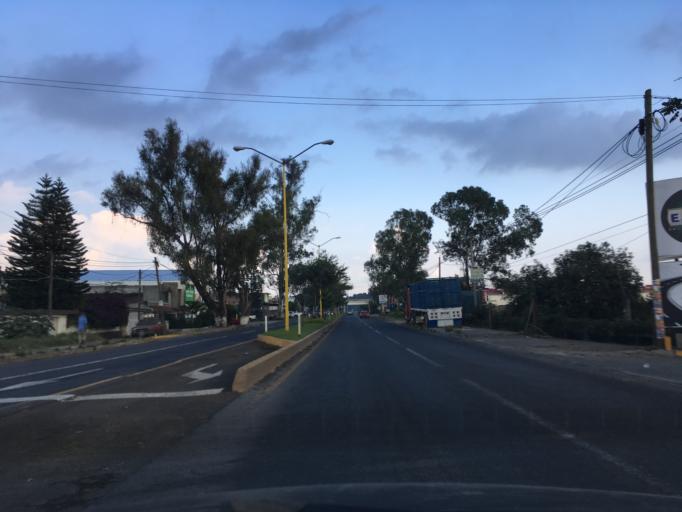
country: MX
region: Michoacan
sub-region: Uruapan
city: Toreo Bajo (El Toreo Bajo)
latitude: 19.4219
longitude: -102.0057
